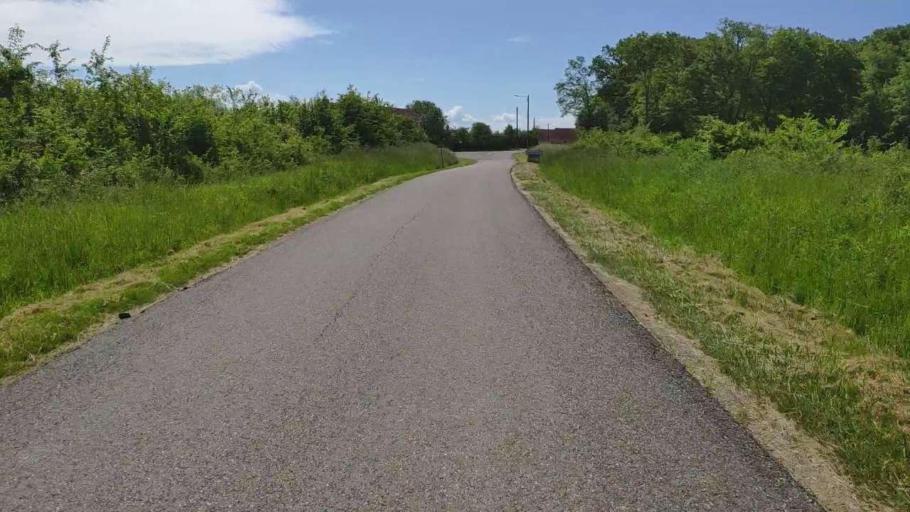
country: FR
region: Franche-Comte
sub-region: Departement du Jura
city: Bletterans
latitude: 46.7077
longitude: 5.4102
